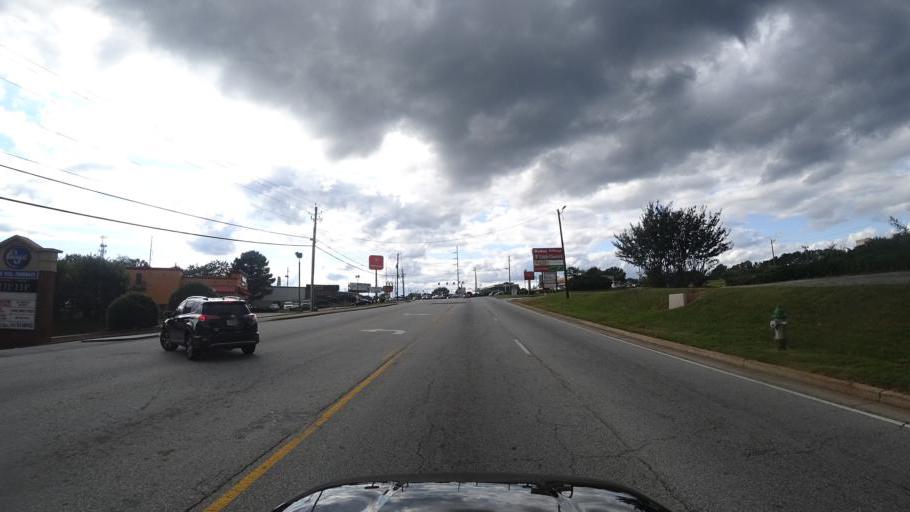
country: US
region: Georgia
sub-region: DeKalb County
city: Stone Mountain
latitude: 33.7610
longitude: -84.1944
